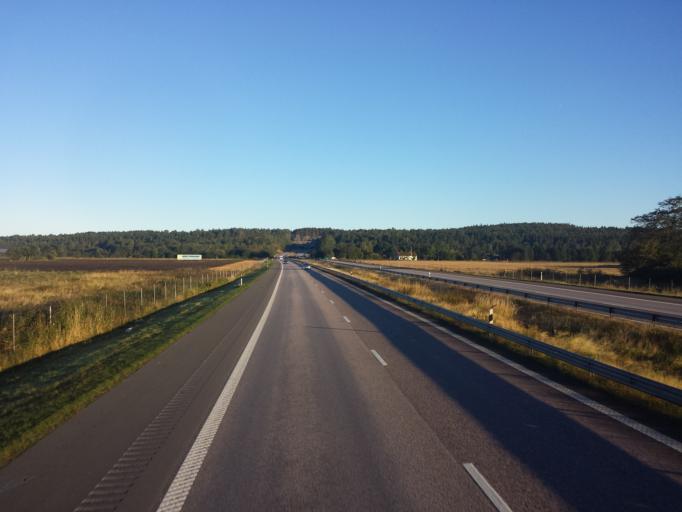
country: SE
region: Halland
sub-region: Varbergs Kommun
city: Veddige
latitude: 57.2242
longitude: 12.2328
